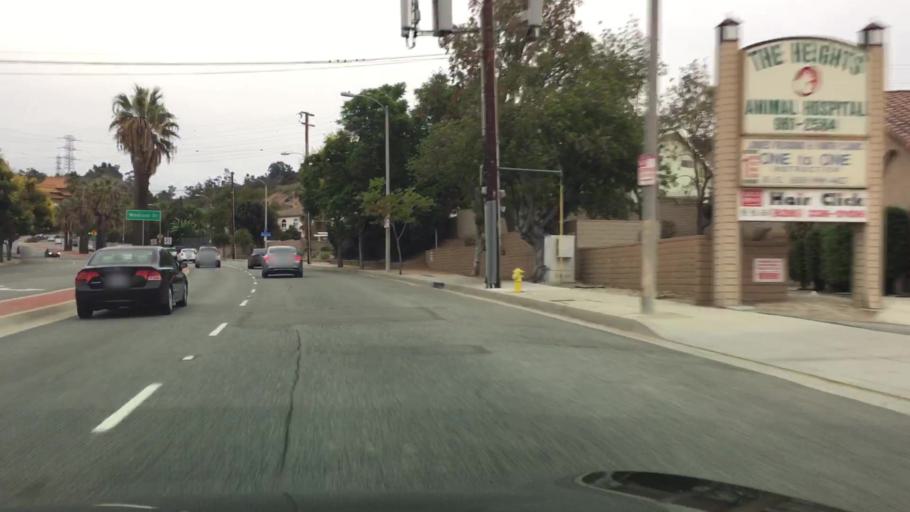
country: US
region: California
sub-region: Los Angeles County
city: Hacienda Heights
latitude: 33.9800
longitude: -117.9726
